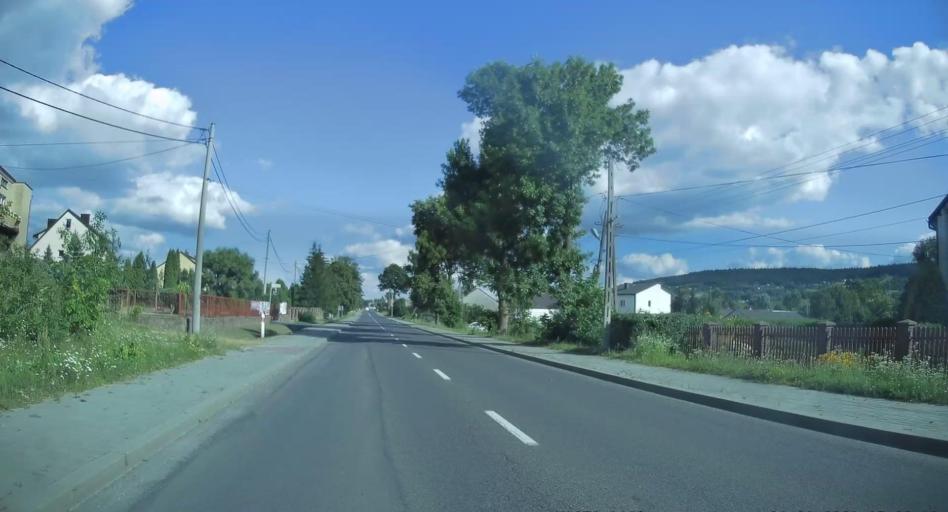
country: PL
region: Swietokrzyskie
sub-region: Powiat kielecki
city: Bodzentyn
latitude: 50.9470
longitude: 20.9356
